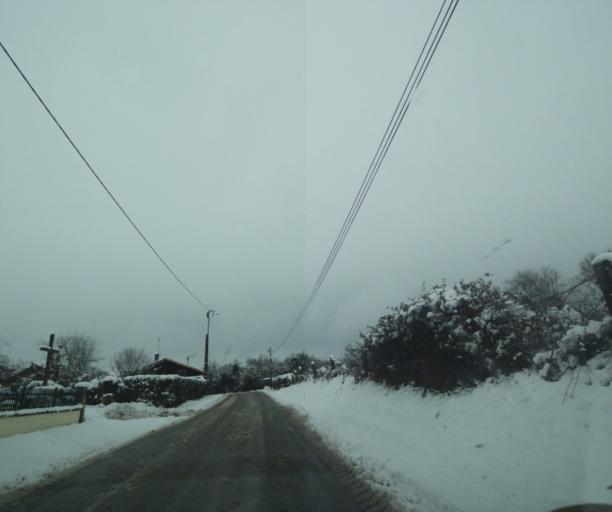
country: FR
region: Champagne-Ardenne
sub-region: Departement de la Haute-Marne
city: Montier-en-Der
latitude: 48.5087
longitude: 4.7824
